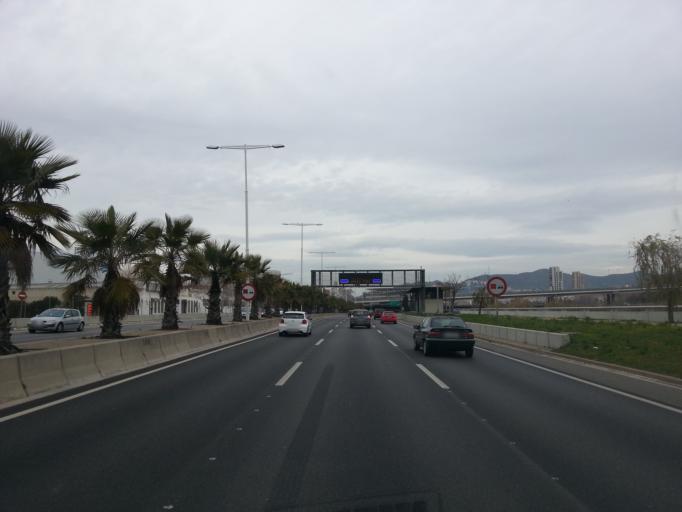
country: ES
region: Catalonia
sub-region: Provincia de Barcelona
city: Sant Adria de Besos
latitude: 41.4331
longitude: 2.2107
